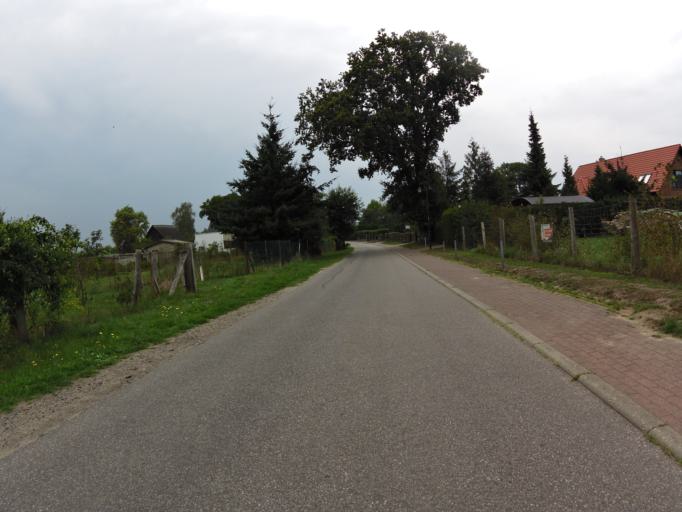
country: DE
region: Mecklenburg-Vorpommern
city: Seebad Heringsdorf
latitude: 53.9199
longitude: 14.1599
